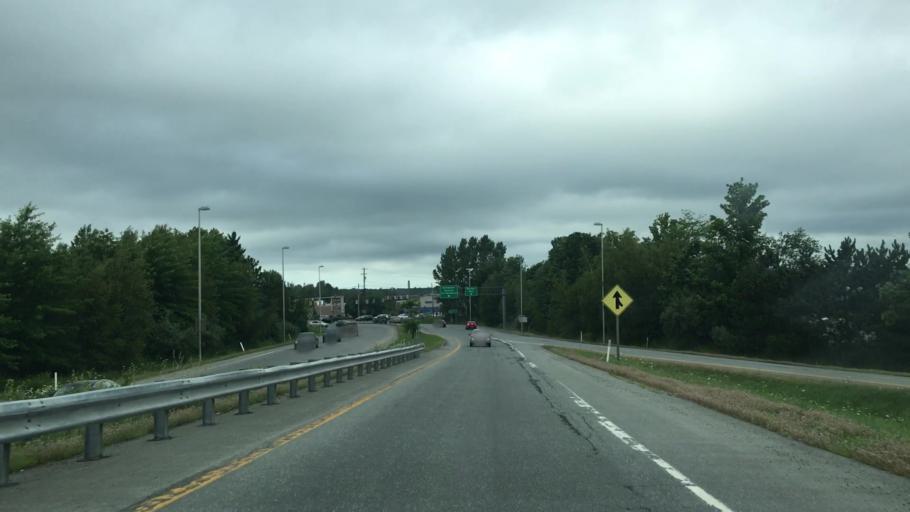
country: US
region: Maine
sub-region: Penobscot County
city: Brewer
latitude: 44.8266
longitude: -68.7543
